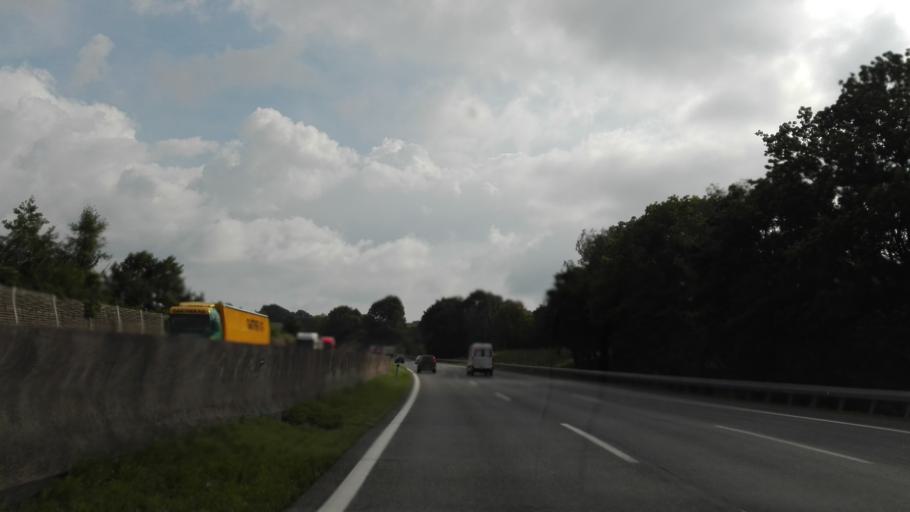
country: AT
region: Lower Austria
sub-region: Politischer Bezirk Melk
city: Erlauf
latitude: 48.1726
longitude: 15.1817
